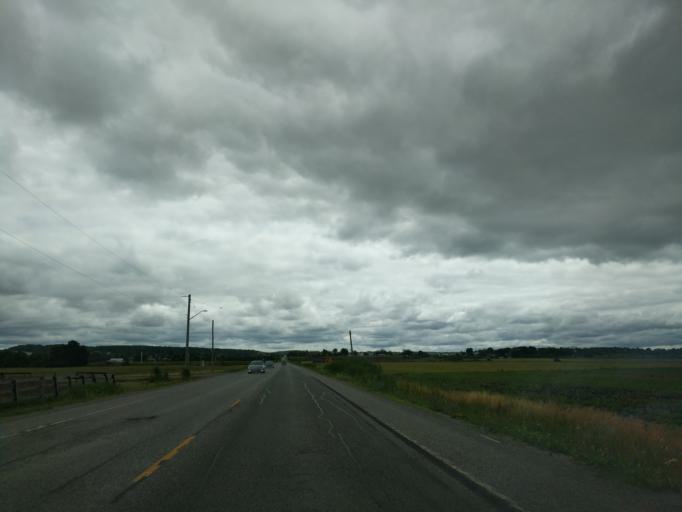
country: CA
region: Ontario
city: Thorold
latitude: 43.1731
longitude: -79.1688
